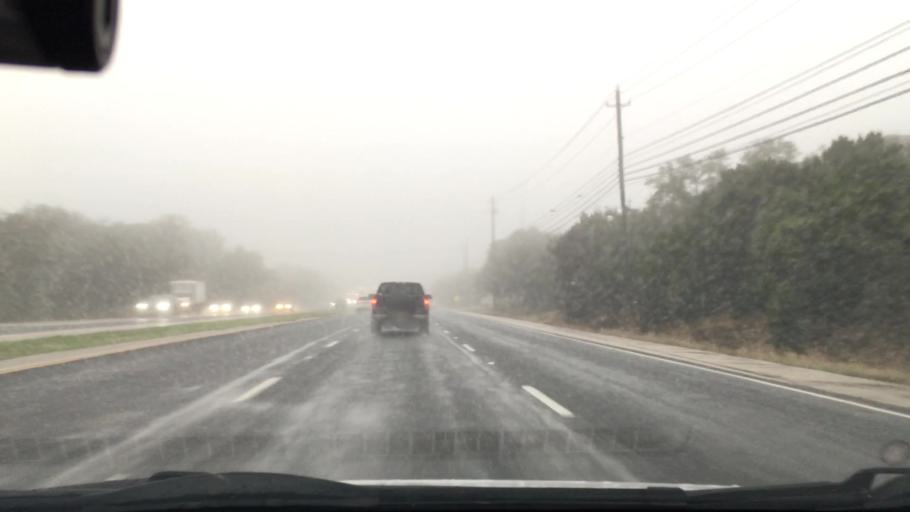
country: US
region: Texas
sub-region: Travis County
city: Barton Creek
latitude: 30.2458
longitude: -97.8452
